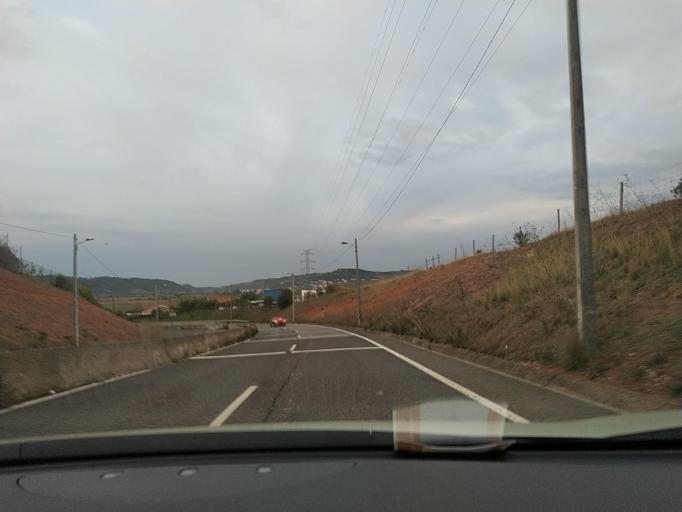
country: PT
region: Lisbon
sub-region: Loures
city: Santo Antao do Tojal
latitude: 38.8617
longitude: -9.1309
